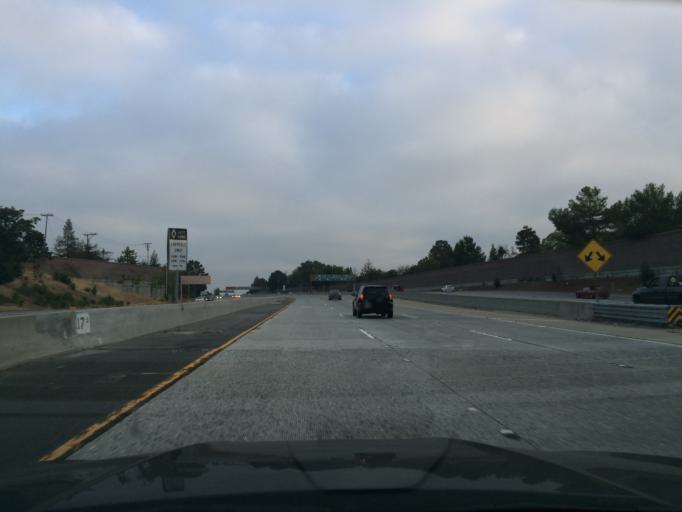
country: US
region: California
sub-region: Santa Clara County
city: Cupertino
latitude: 37.3245
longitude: -122.0504
